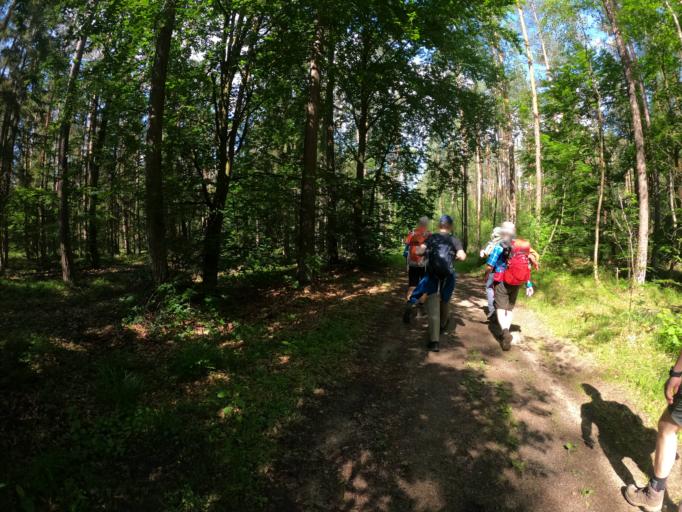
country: DE
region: Bavaria
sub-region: Upper Franconia
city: Strullendorf
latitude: 49.8826
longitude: 10.9602
